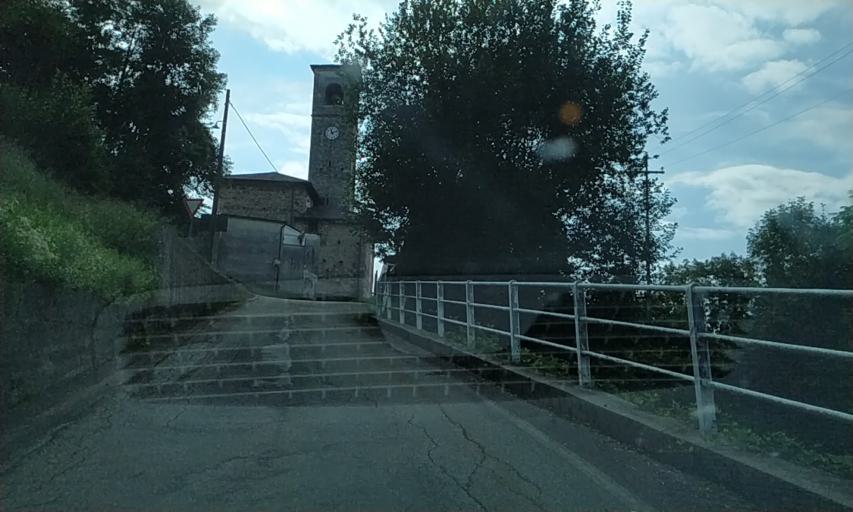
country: IT
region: Piedmont
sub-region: Provincia di Biella
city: Frazione Chiesa
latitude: 45.6936
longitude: 8.2123
